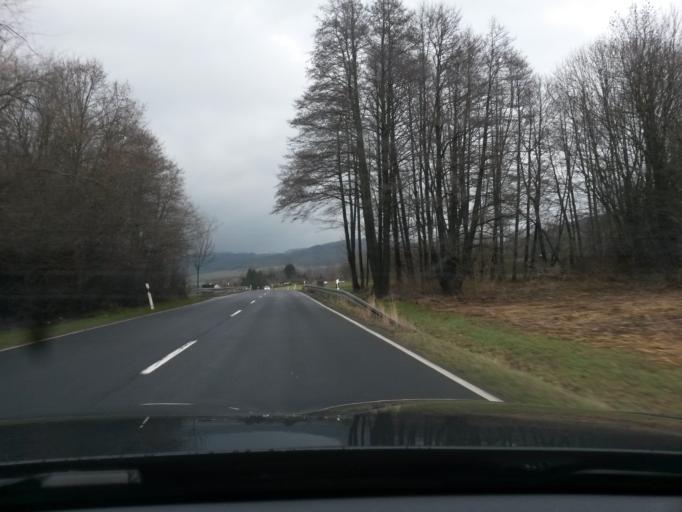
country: DE
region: Thuringia
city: Birx
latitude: 50.5065
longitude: 10.0125
